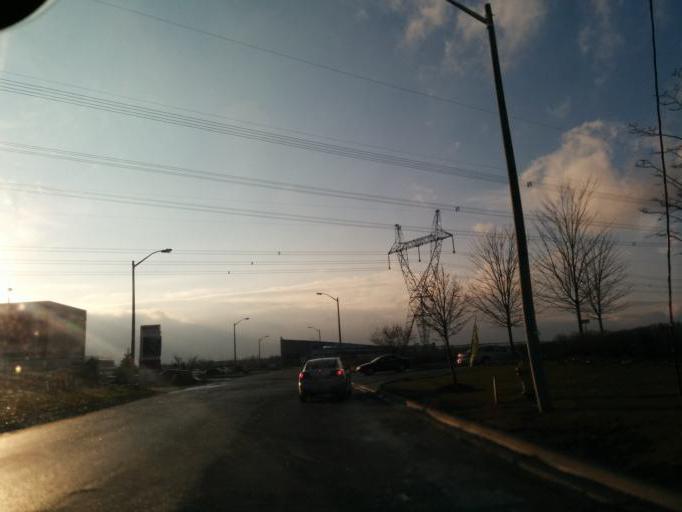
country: CA
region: Ontario
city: Vaughan
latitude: 43.7839
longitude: -79.6262
